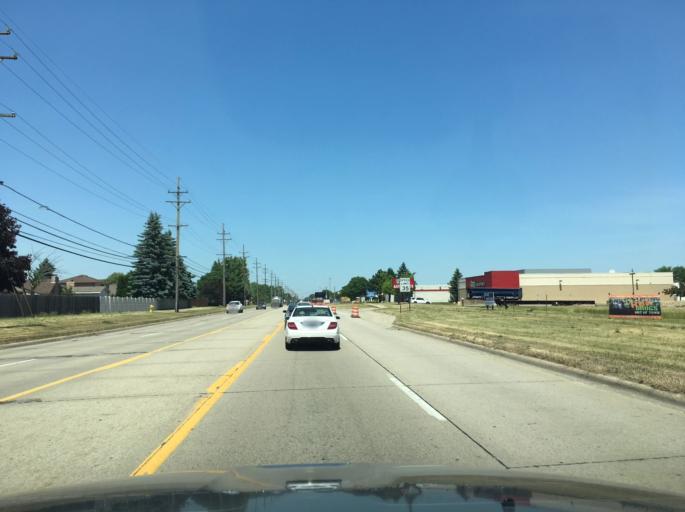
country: US
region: Michigan
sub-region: Macomb County
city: Clinton
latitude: 42.5947
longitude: -82.9522
